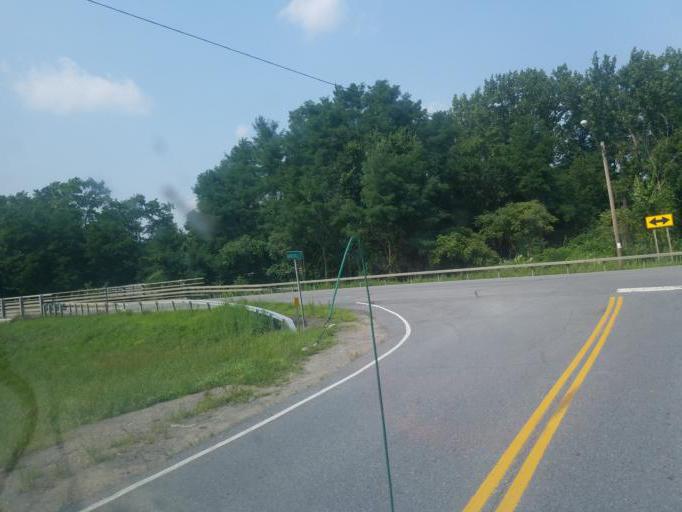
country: US
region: New York
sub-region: Montgomery County
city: Tribes Hill
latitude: 42.9298
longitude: -74.3160
